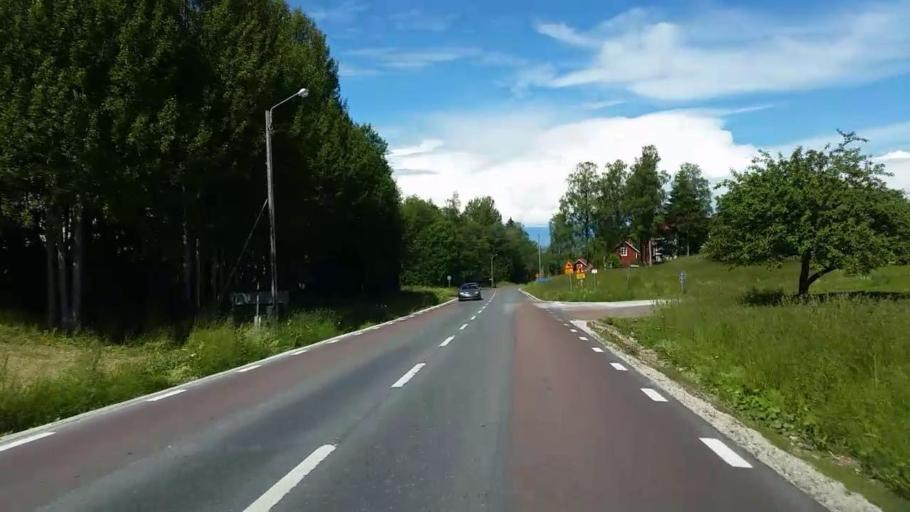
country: SE
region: Dalarna
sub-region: Rattviks Kommun
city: Raettvik
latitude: 61.0419
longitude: 15.1952
